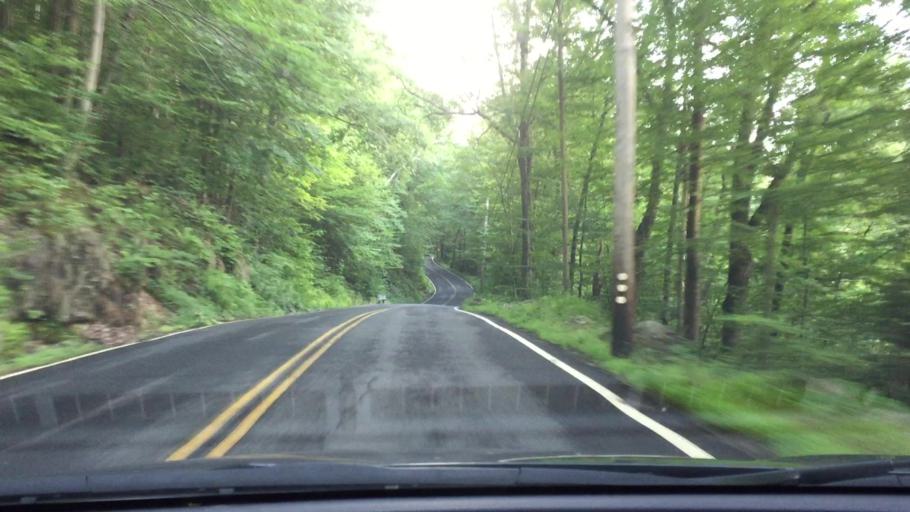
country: US
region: Massachusetts
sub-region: Hampshire County
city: Southampton
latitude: 42.1986
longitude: -72.8464
